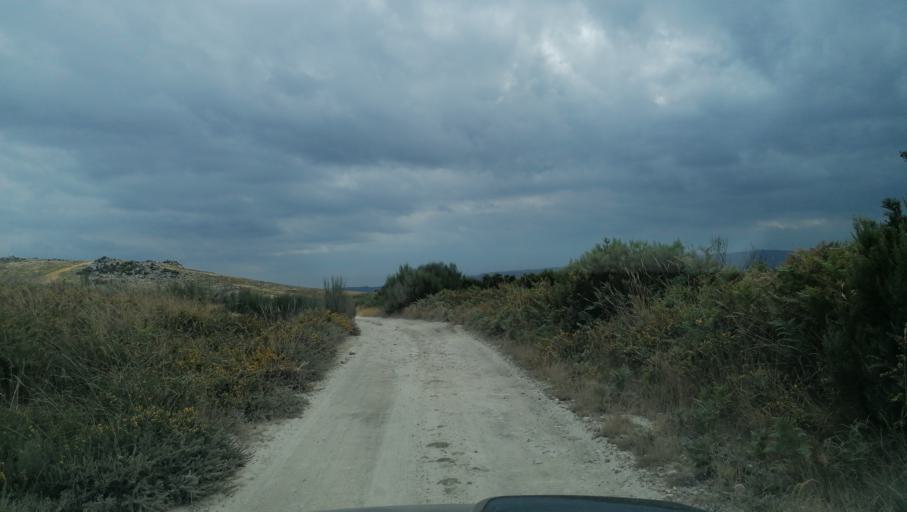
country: PT
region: Vila Real
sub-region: Vila Pouca de Aguiar
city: Vila Pouca de Aguiar
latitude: 41.5358
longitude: -7.6988
